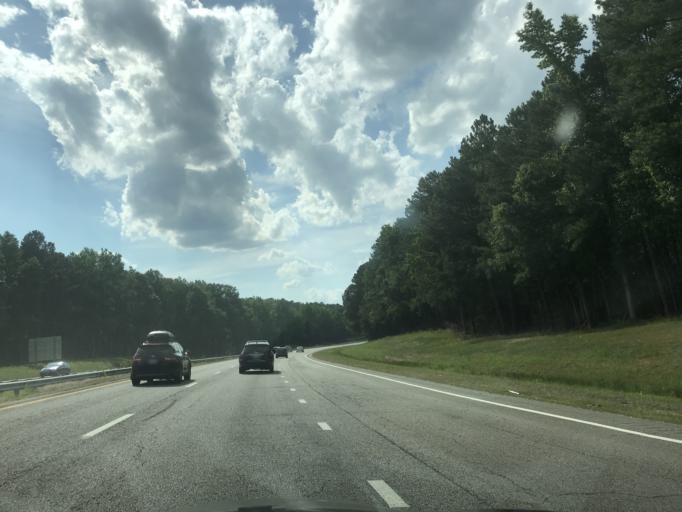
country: US
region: North Carolina
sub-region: Nash County
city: Nashville
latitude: 35.9731
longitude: -77.9441
